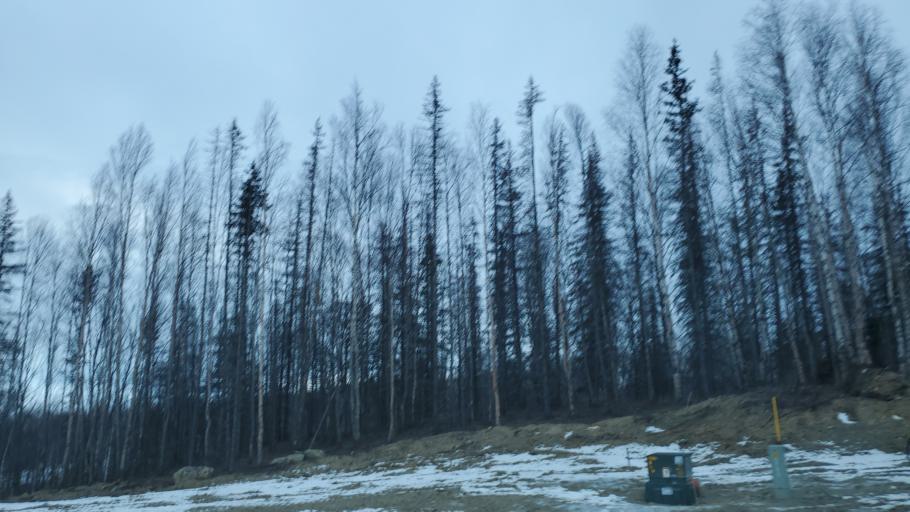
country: US
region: Alaska
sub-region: Matanuska-Susitna Borough
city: Gateway
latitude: 61.6566
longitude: -149.2329
